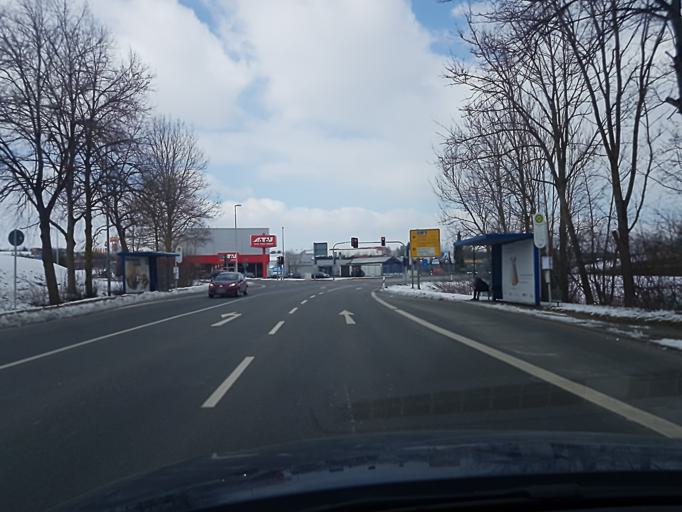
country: DE
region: Baden-Wuerttemberg
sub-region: Karlsruhe Region
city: Horb am Neckar
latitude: 48.4550
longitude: 8.7006
